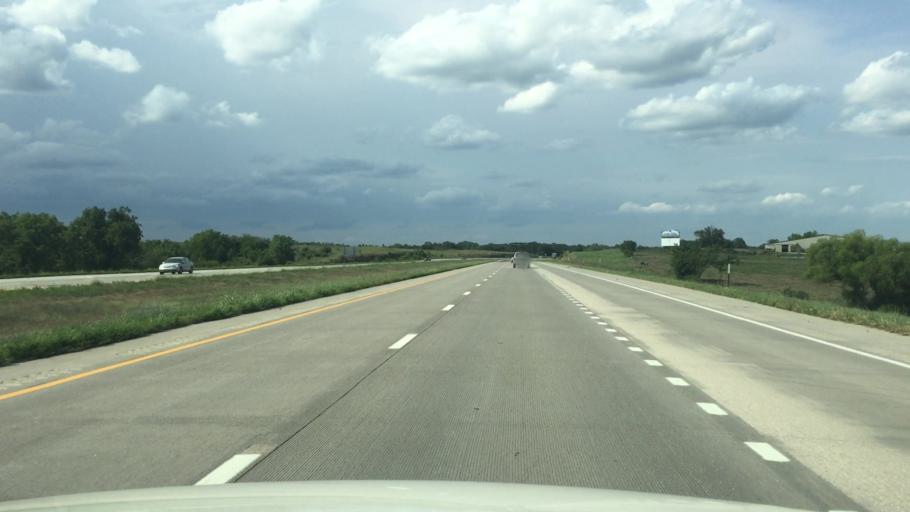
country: US
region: Kansas
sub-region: Miami County
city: Louisburg
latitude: 38.5659
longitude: -94.6945
